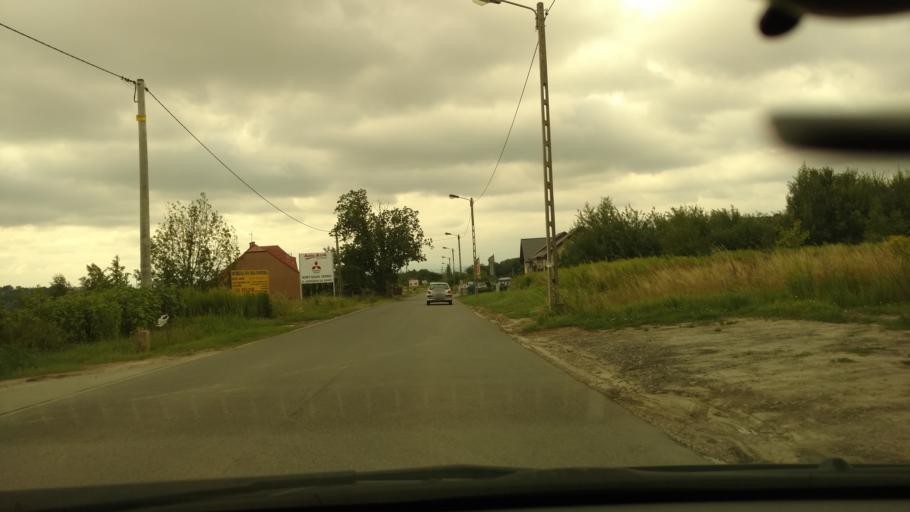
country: PL
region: Lesser Poland Voivodeship
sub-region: Powiat krakowski
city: Zielonki
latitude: 50.1168
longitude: 19.9420
